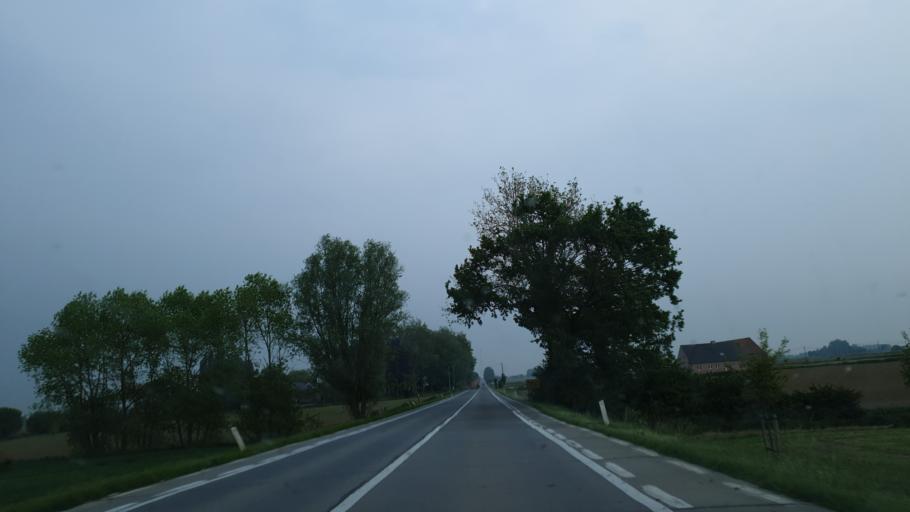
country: BE
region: Flanders
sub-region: Provincie West-Vlaanderen
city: Alveringem
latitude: 50.9698
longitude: 2.7017
